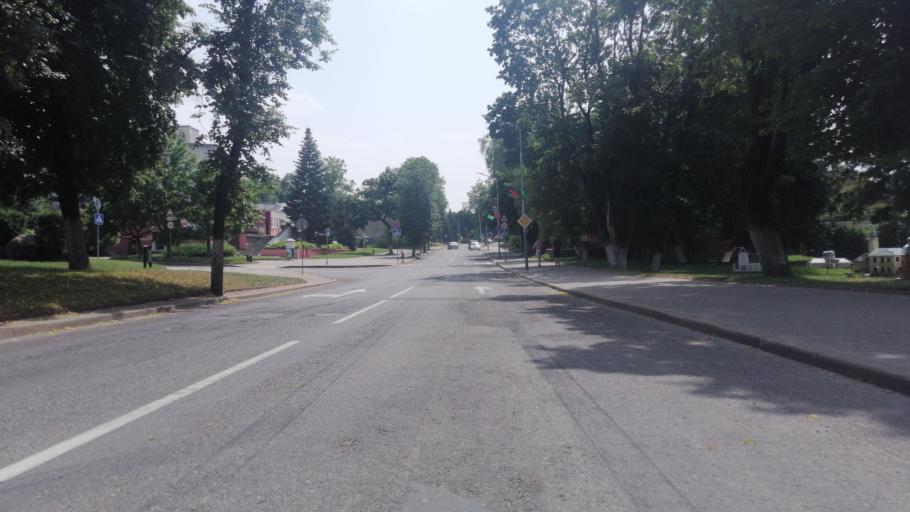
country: BY
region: Grodnenskaya
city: Navahrudak
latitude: 53.5965
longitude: 25.8225
